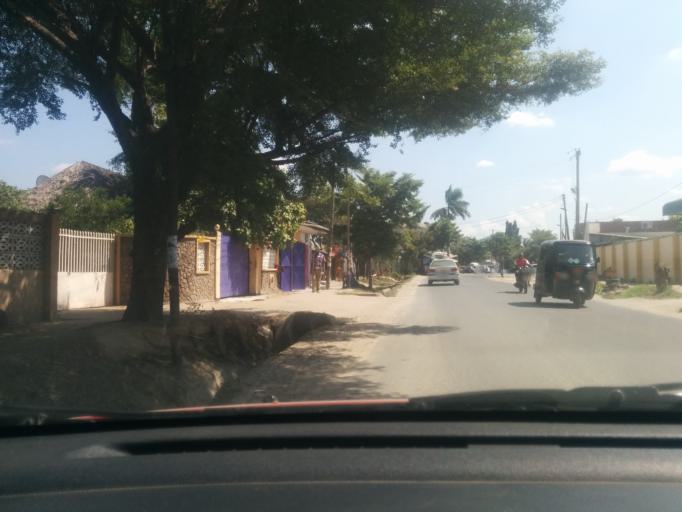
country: TZ
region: Dar es Salaam
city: Magomeni
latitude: -6.7802
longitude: 39.2216
